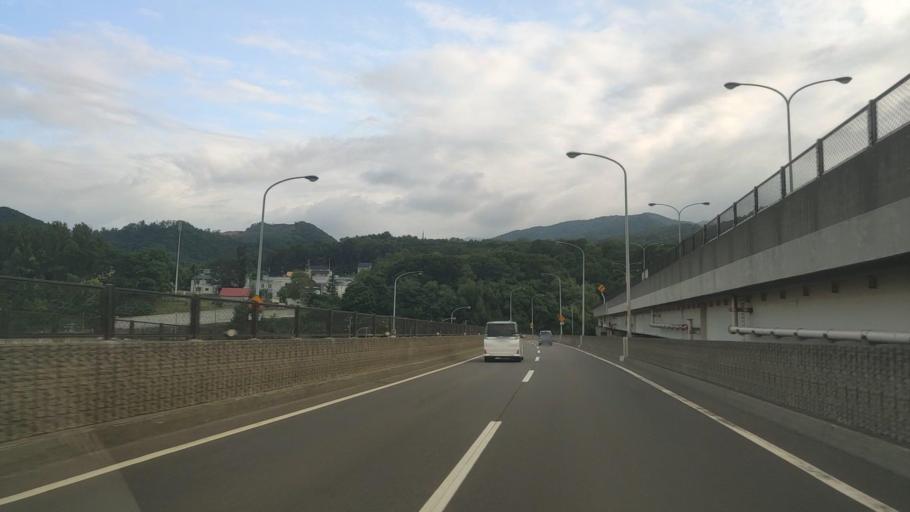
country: JP
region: Hokkaido
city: Otaru
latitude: 43.1364
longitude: 141.1780
